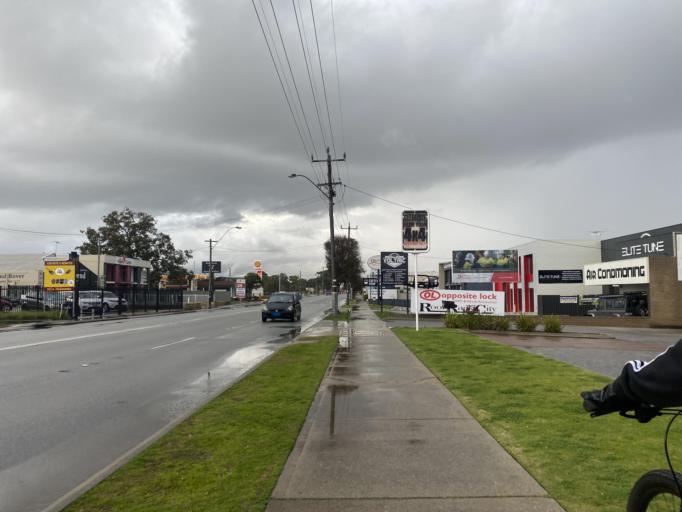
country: AU
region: Western Australia
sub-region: Canning
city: Bentley
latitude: -31.9941
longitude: 115.9179
